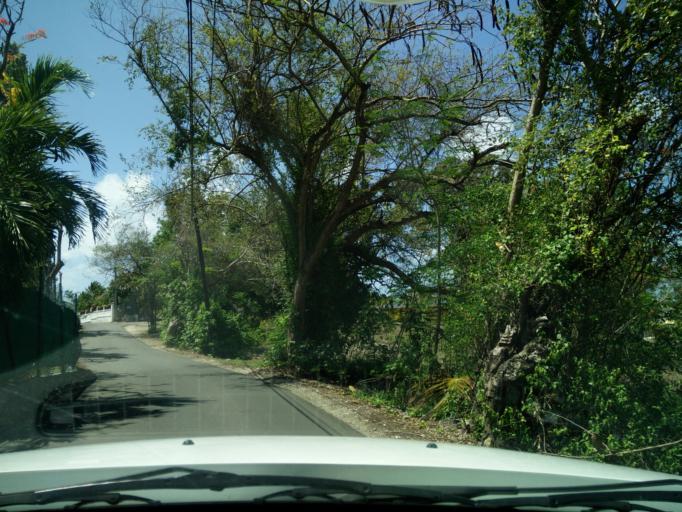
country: GP
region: Guadeloupe
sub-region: Guadeloupe
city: Sainte-Anne
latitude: 16.2466
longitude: -61.3447
